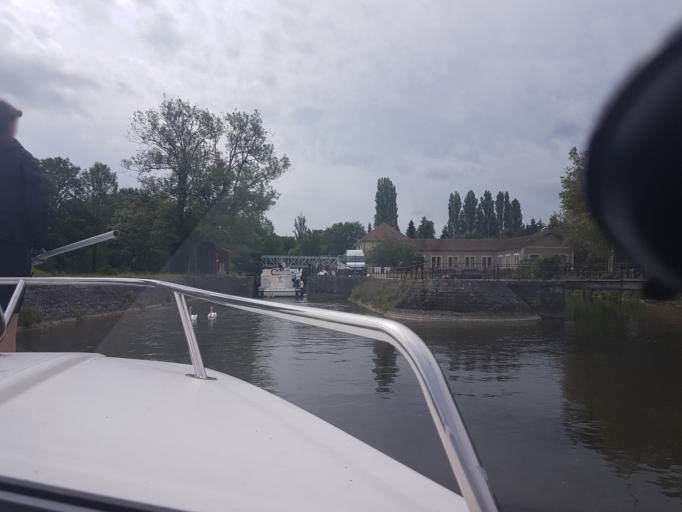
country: FR
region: Bourgogne
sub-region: Departement de l'Yonne
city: Auxerre
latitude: 47.7944
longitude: 3.5818
